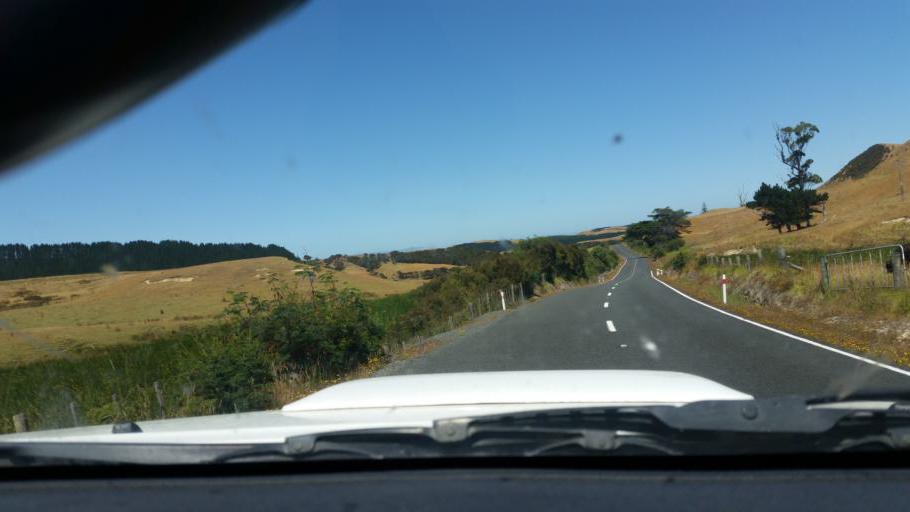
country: NZ
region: Northland
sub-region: Kaipara District
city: Dargaville
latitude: -35.8248
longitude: 173.6786
